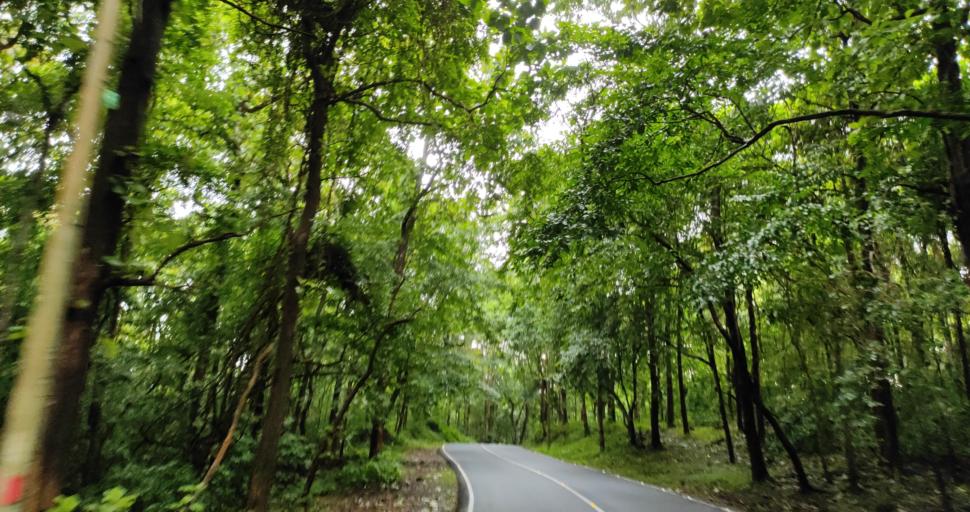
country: IN
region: Kerala
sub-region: Thrissur District
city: Kizhake Chalakudi
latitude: 10.3005
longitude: 76.4431
